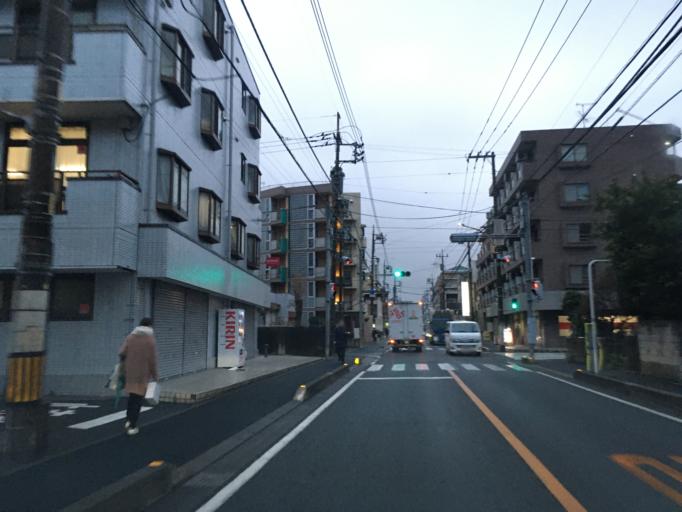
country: JP
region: Saitama
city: Wako
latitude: 35.7844
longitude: 139.6080
